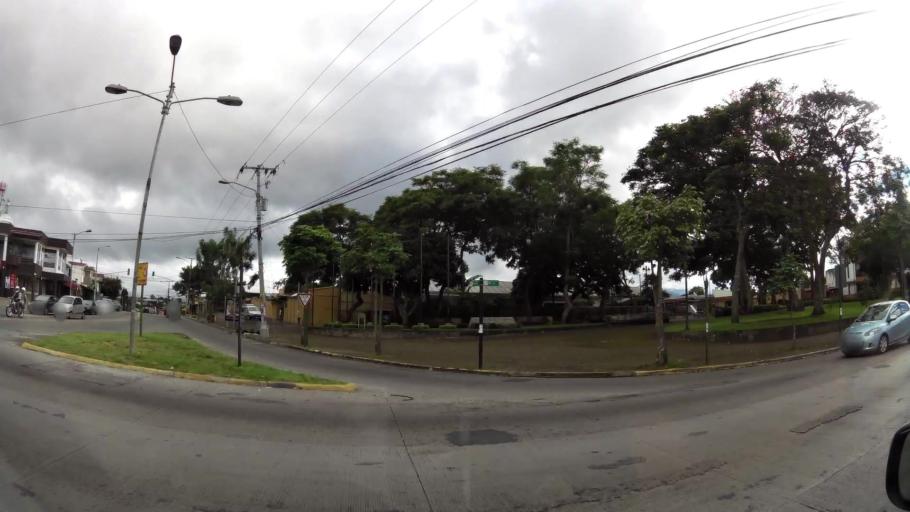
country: CR
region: San Jose
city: San Pedro
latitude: 9.9108
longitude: -84.0575
